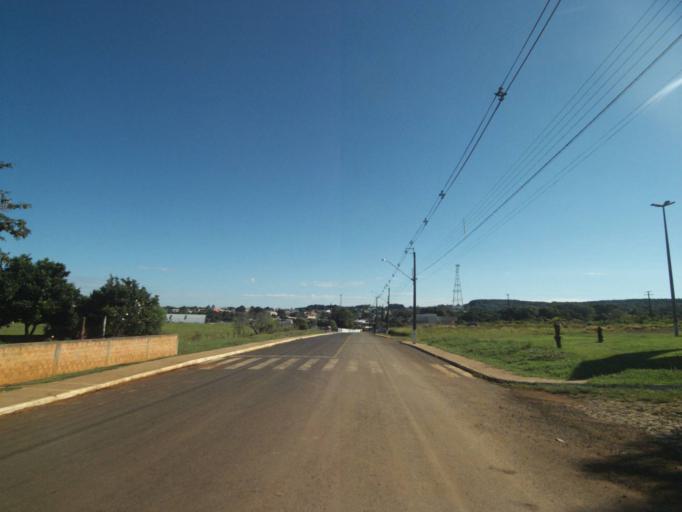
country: BR
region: Parana
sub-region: Pinhao
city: Pinhao
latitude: -25.8435
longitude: -52.0308
